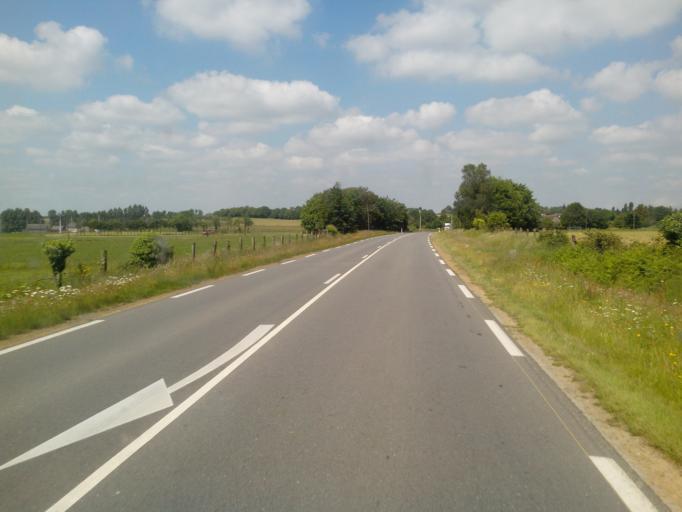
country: FR
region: Brittany
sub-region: Departement d'Ille-et-Vilaine
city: Saint-Germain-en-Cogles
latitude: 48.3936
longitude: -1.2892
